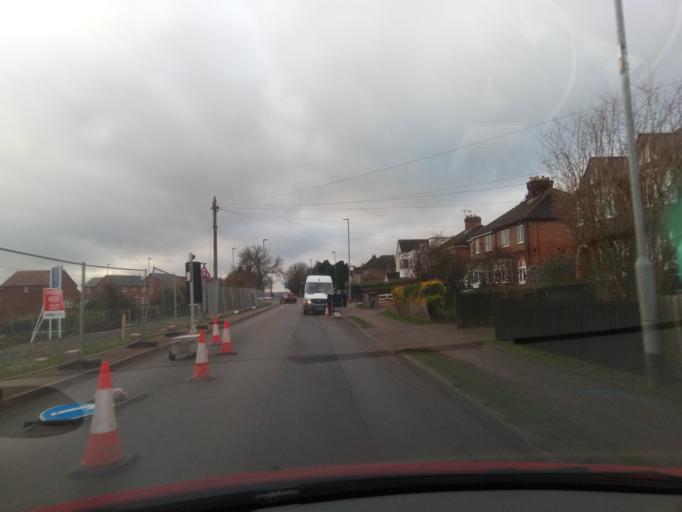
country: GB
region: England
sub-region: Leicestershire
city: Sileby
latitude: 52.7410
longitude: -1.1013
